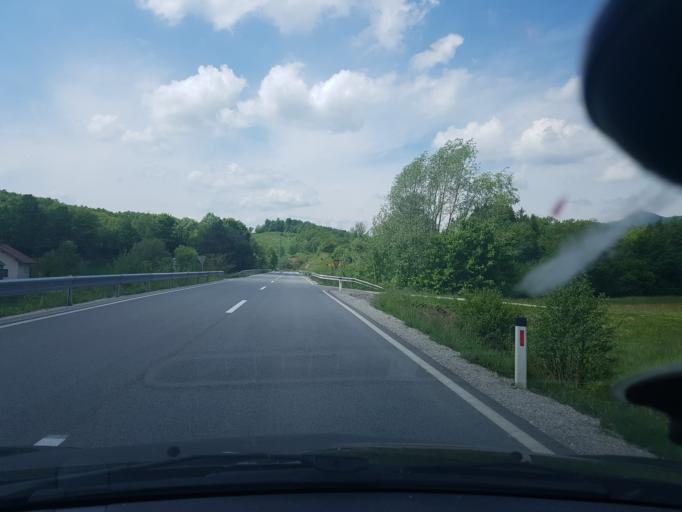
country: SI
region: Rogaska Slatina
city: Rogaska Slatina
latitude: 46.2424
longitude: 15.6604
